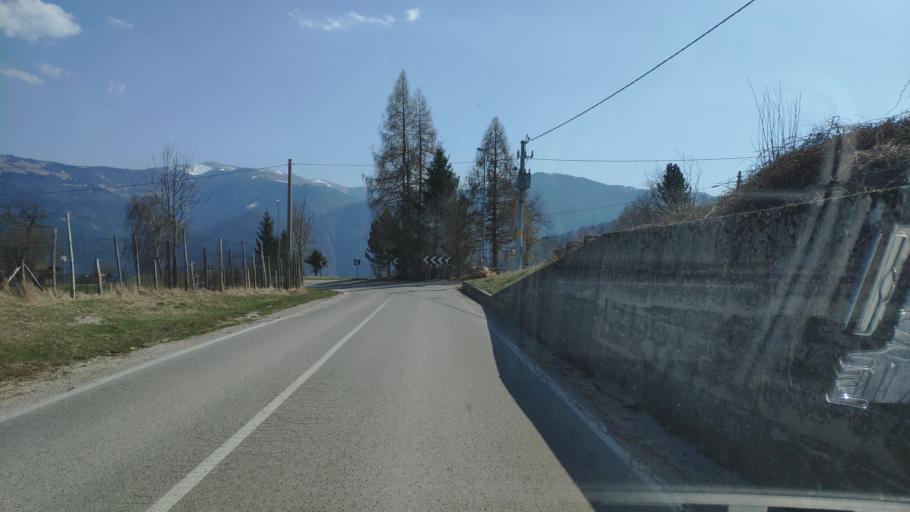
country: IT
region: Veneto
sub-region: Provincia di Vicenza
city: Enego
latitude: 45.9294
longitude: 11.7025
